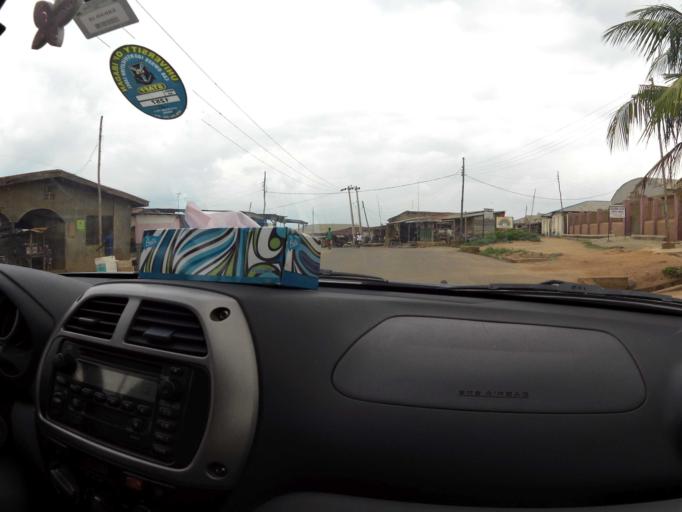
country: NG
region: Oyo
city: Moniya
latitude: 7.5251
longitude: 3.9226
